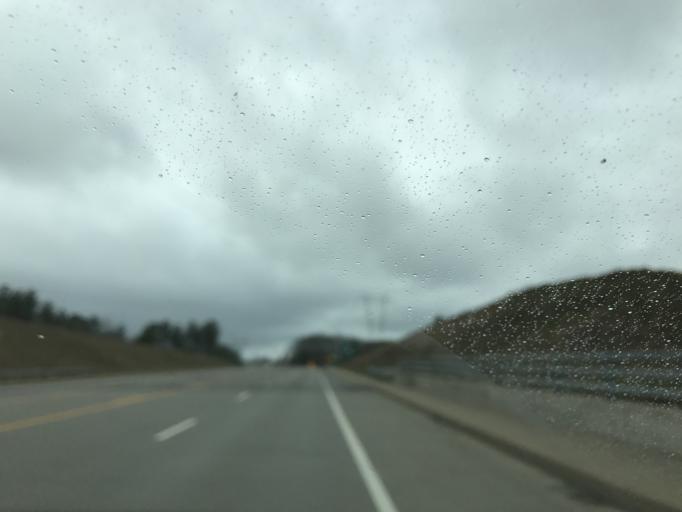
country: US
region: West Virginia
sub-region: Raleigh County
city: Beckley
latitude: 37.7925
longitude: -81.1655
